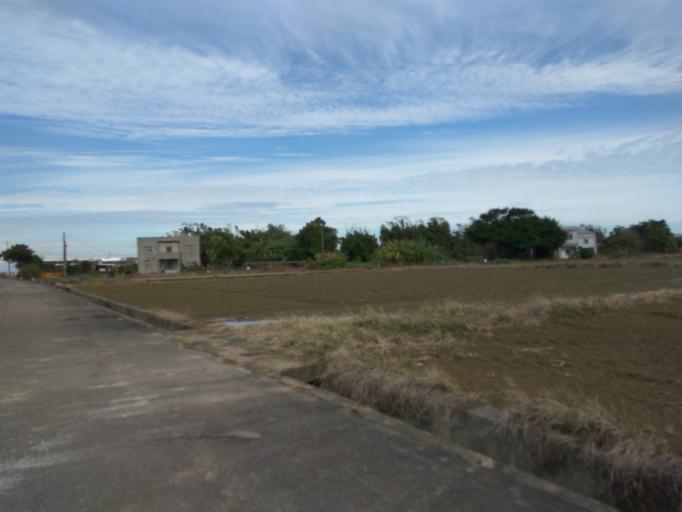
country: TW
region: Taiwan
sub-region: Hsinchu
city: Zhubei
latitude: 24.9853
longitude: 121.0899
